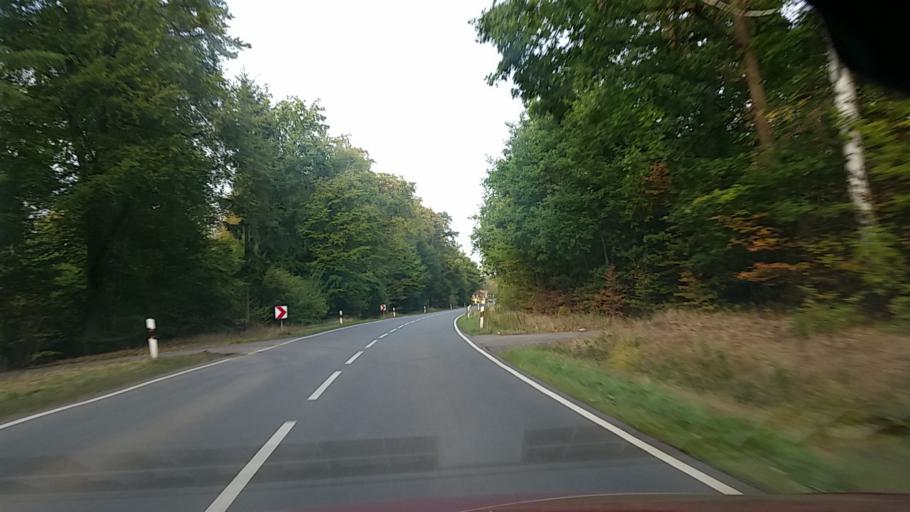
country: DE
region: Lower Saxony
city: Hohne
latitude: 52.5902
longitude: 10.3336
